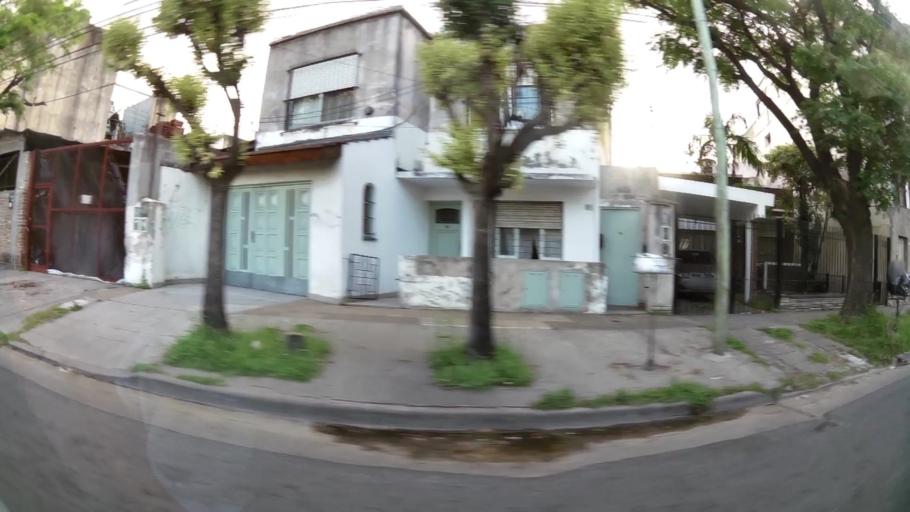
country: AR
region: Buenos Aires
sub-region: Partido de General San Martin
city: General San Martin
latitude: -34.5826
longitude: -58.5205
